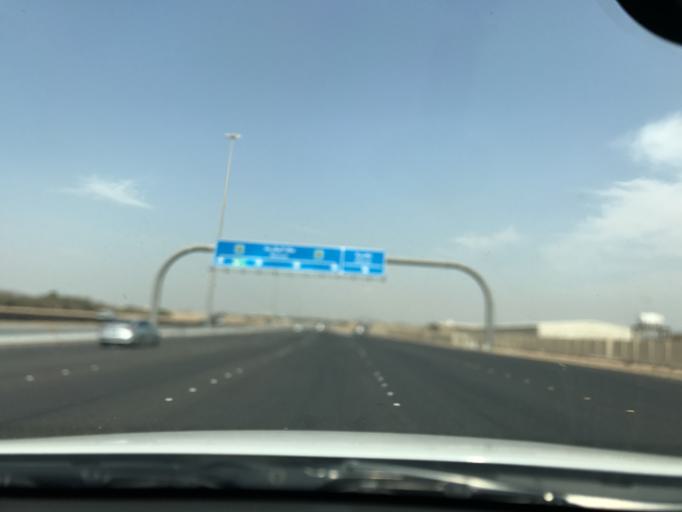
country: SA
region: Makkah
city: Jeddah
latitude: 21.3890
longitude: 39.4204
